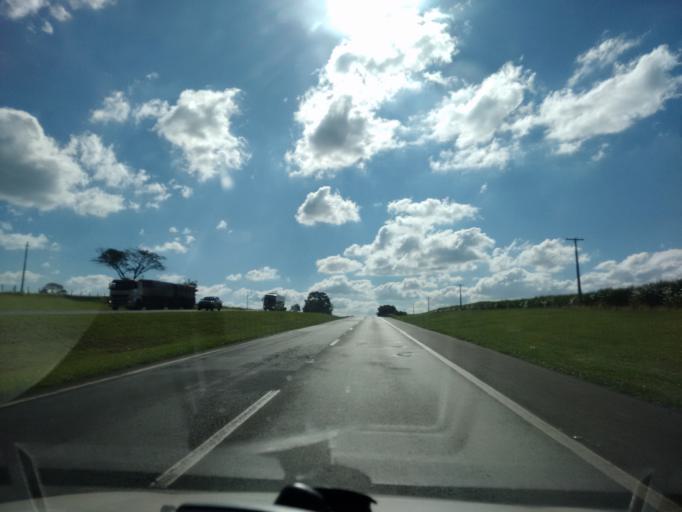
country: BR
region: Sao Paulo
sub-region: Ibate
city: Ibate
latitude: -21.9085
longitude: -48.0509
